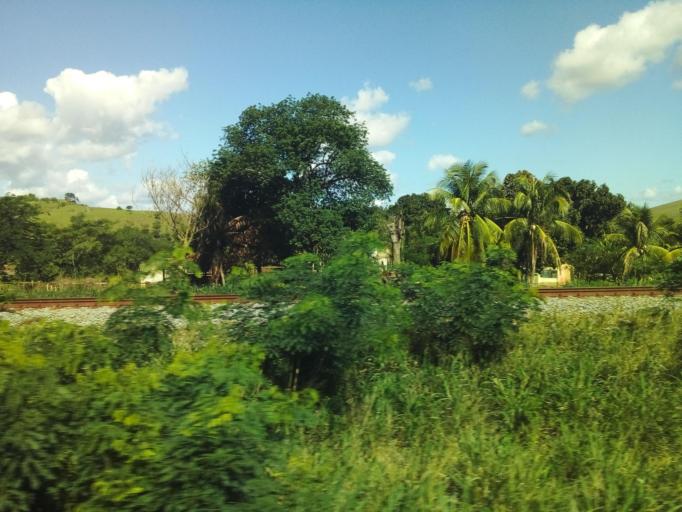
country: BR
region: Minas Gerais
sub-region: Governador Valadares
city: Governador Valadares
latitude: -18.8544
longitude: -41.8621
